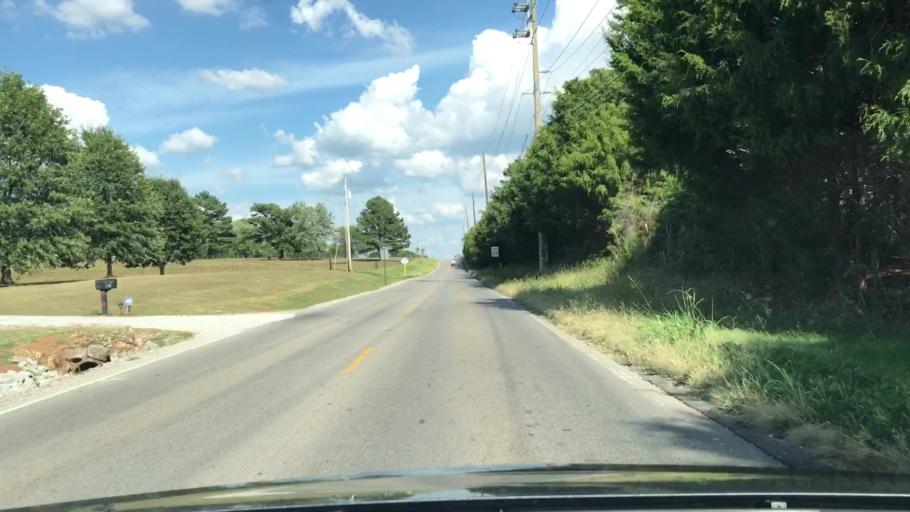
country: US
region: Alabama
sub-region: Madison County
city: Harvest
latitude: 34.8085
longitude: -86.7392
